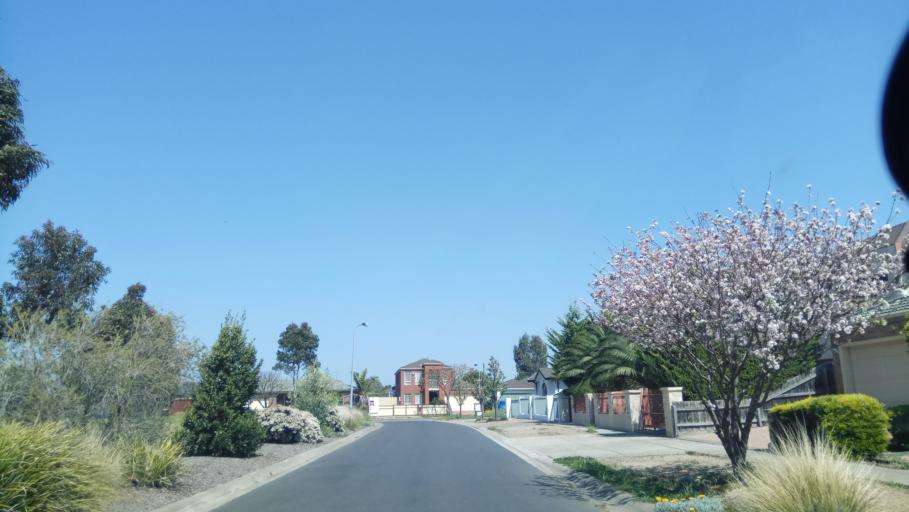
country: AU
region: Victoria
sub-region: Wyndham
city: Williams Landing
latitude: -37.8838
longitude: 144.7537
